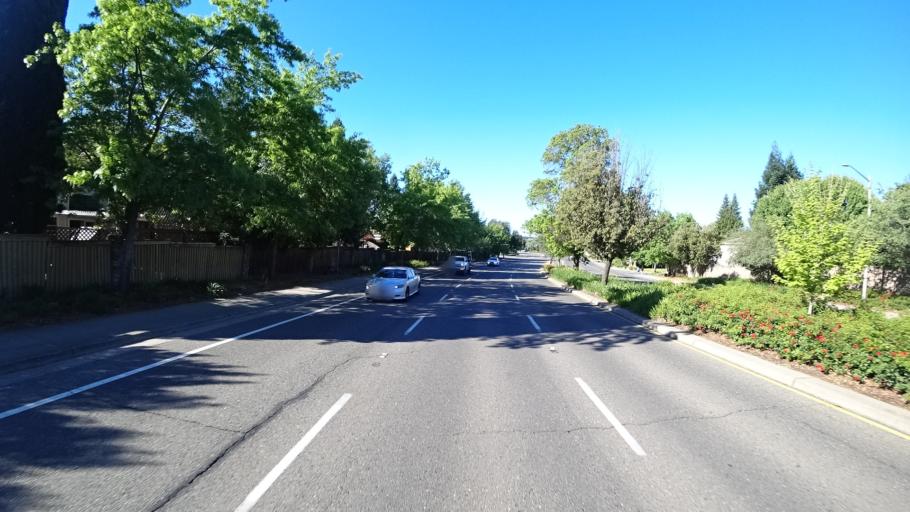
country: US
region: California
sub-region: Placer County
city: Rocklin
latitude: 38.8171
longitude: -121.2560
